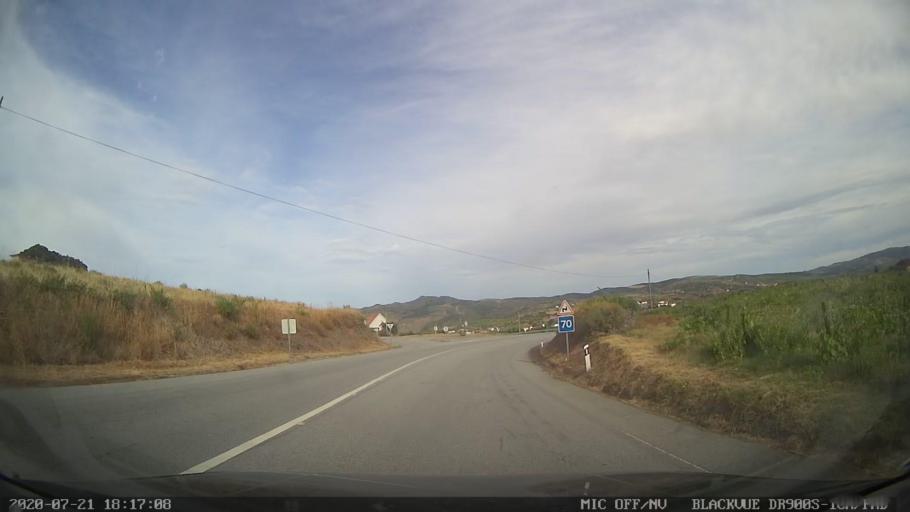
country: PT
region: Viseu
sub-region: Sao Joao da Pesqueira
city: Sao Joao da Pesqueira
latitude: 41.1064
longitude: -7.3870
